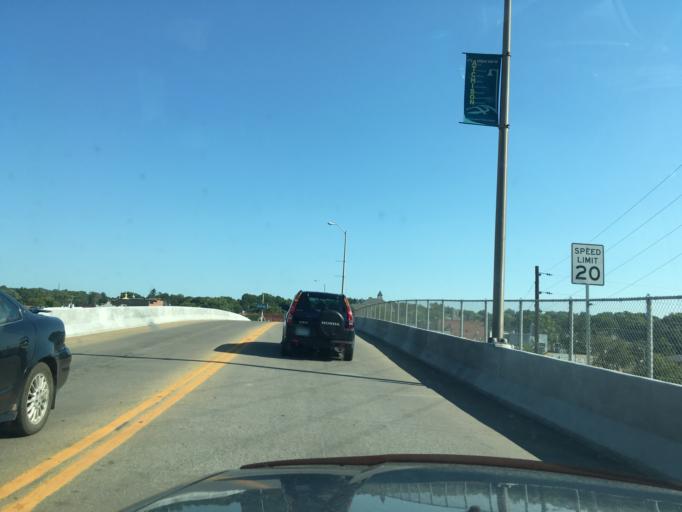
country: US
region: Kansas
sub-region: Atchison County
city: Atchison
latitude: 39.5598
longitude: -95.1205
